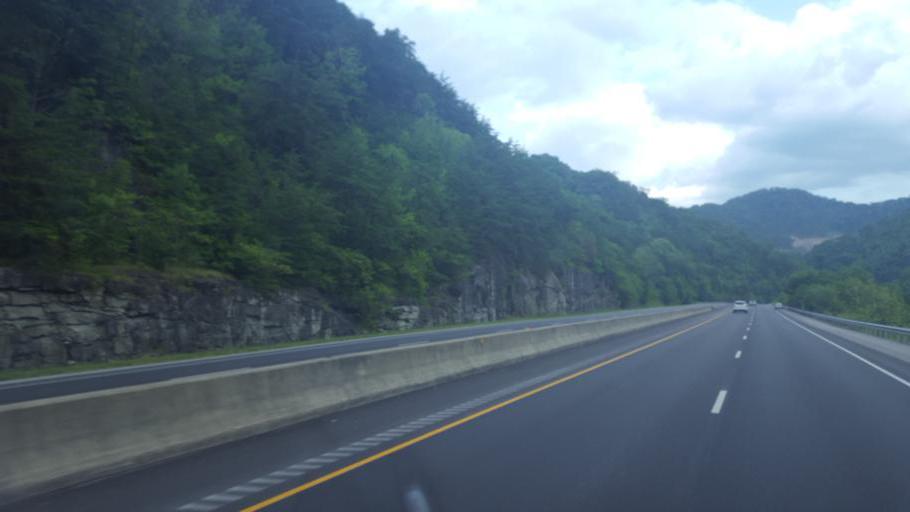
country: US
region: Kentucky
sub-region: Pike County
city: Pikeville
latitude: 37.3512
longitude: -82.5524
